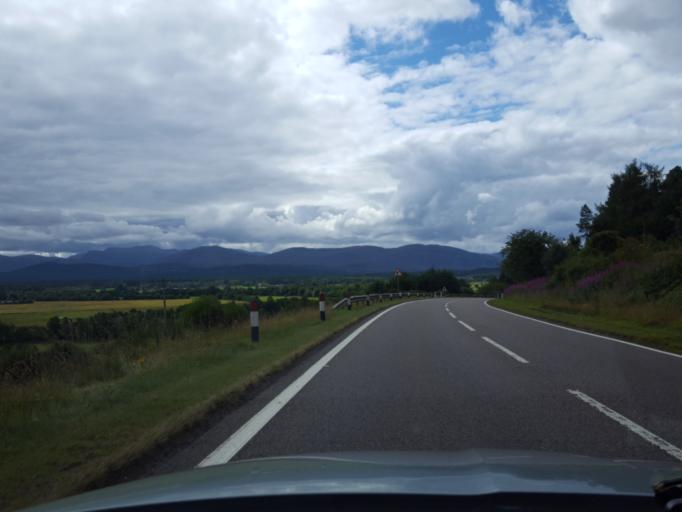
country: GB
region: Scotland
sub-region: Highland
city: Grantown on Spey
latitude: 57.2842
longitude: -3.6689
